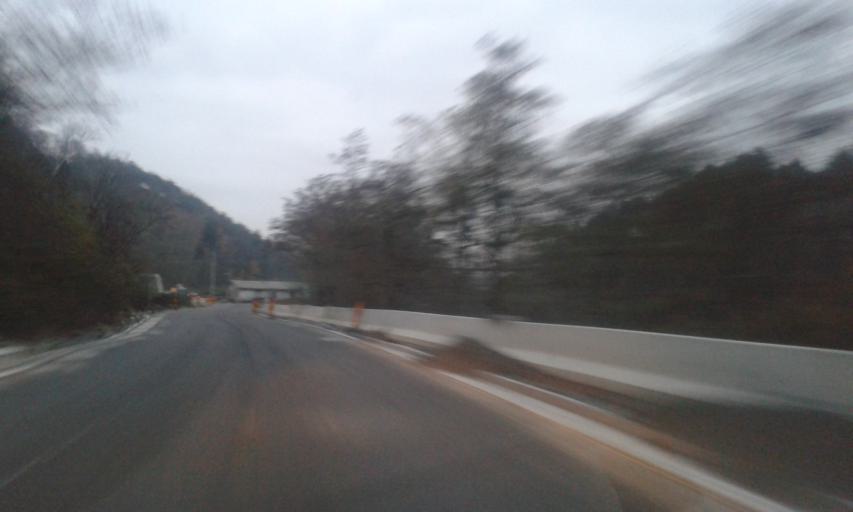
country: RO
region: Gorj
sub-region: Comuna Bumbesti-Jiu
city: Bumbesti-Jiu
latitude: 45.1907
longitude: 23.3919
